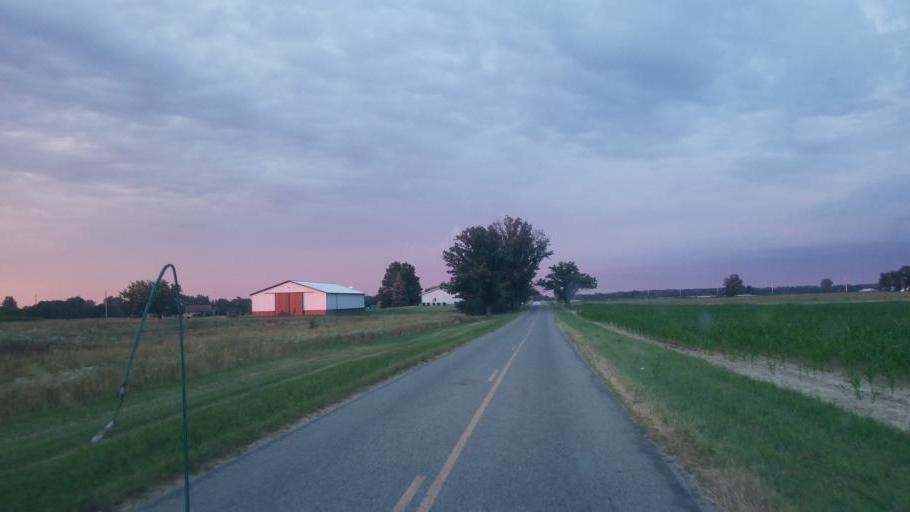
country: US
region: Ohio
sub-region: Defiance County
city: Hicksville
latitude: 41.3270
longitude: -84.8040
